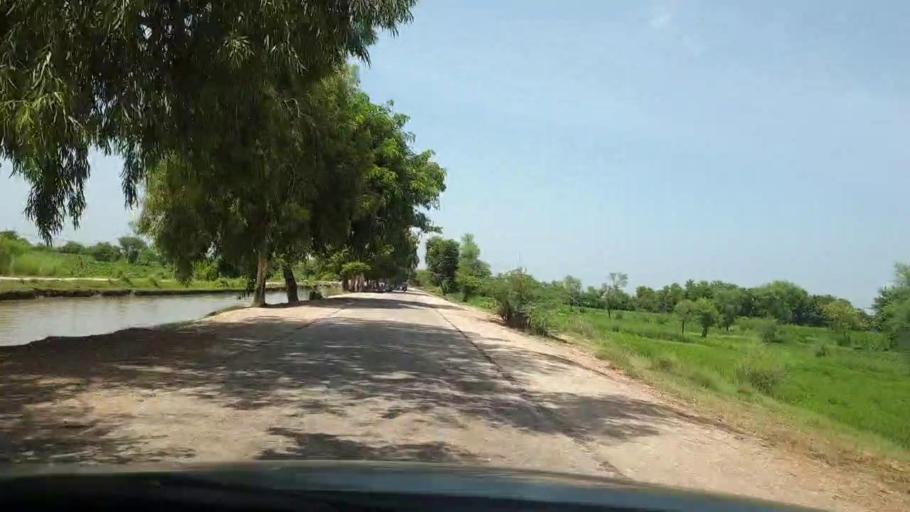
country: PK
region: Sindh
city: Pano Aqil
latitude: 27.6948
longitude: 69.1109
